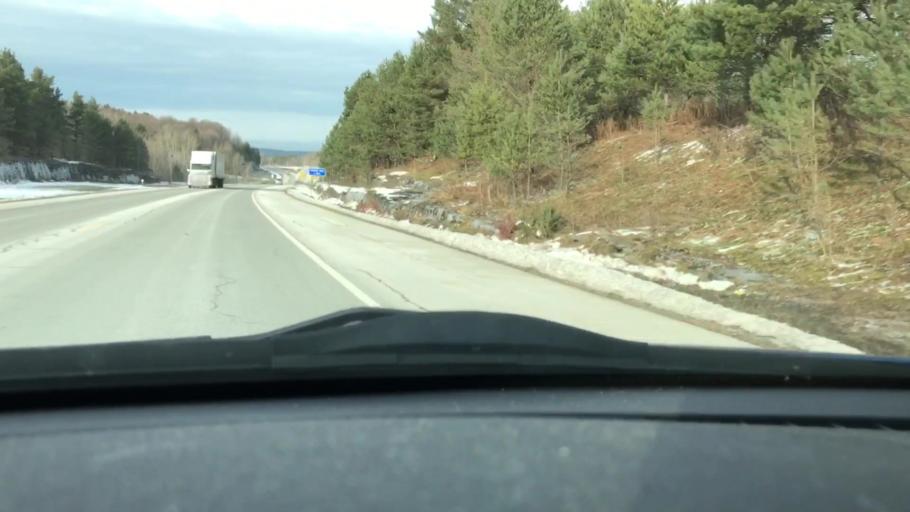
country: US
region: New York
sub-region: Oneida County
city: Boonville
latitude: 43.5226
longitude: -75.3256
